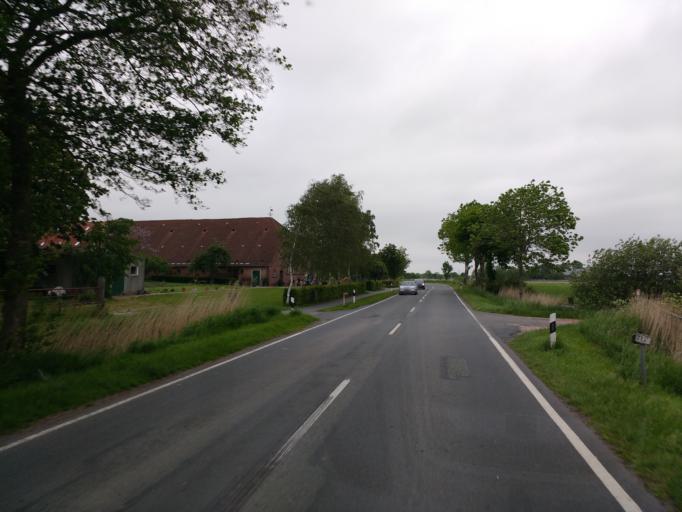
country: DE
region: Lower Saxony
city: Jever
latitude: 53.6453
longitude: 7.9241
